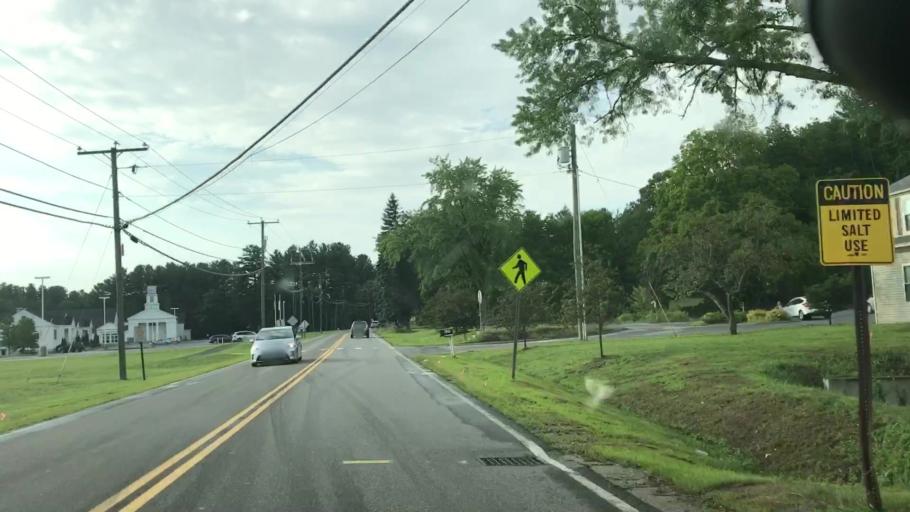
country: US
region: New Hampshire
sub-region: Hillsborough County
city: Hollis
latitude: 42.8039
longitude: -71.5542
